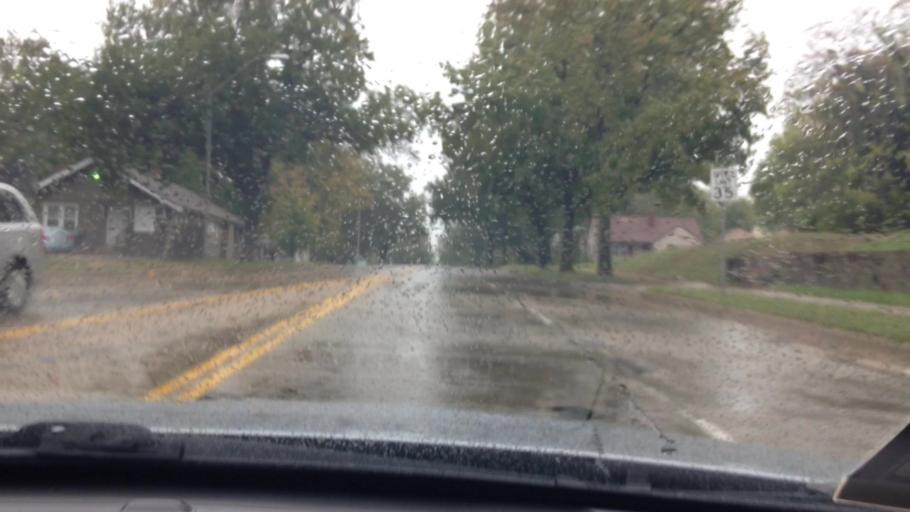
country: US
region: Kansas
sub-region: Johnson County
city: Mission Hills
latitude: 38.9979
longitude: -94.5544
